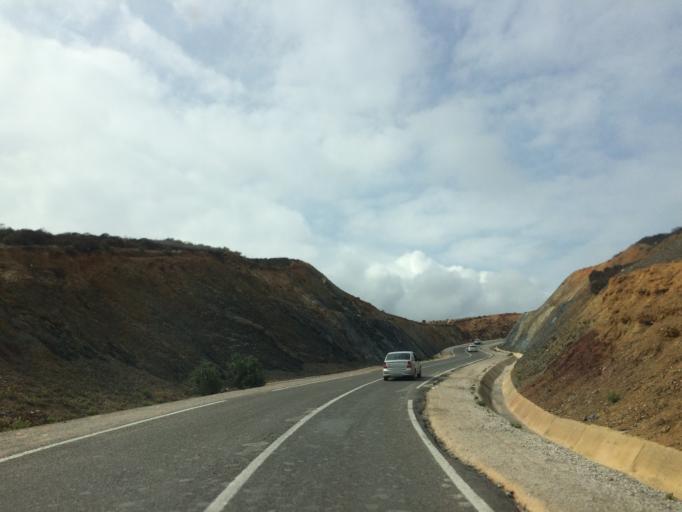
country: ES
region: Ceuta
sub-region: Ceuta
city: Ceuta
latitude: 35.8666
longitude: -5.3481
